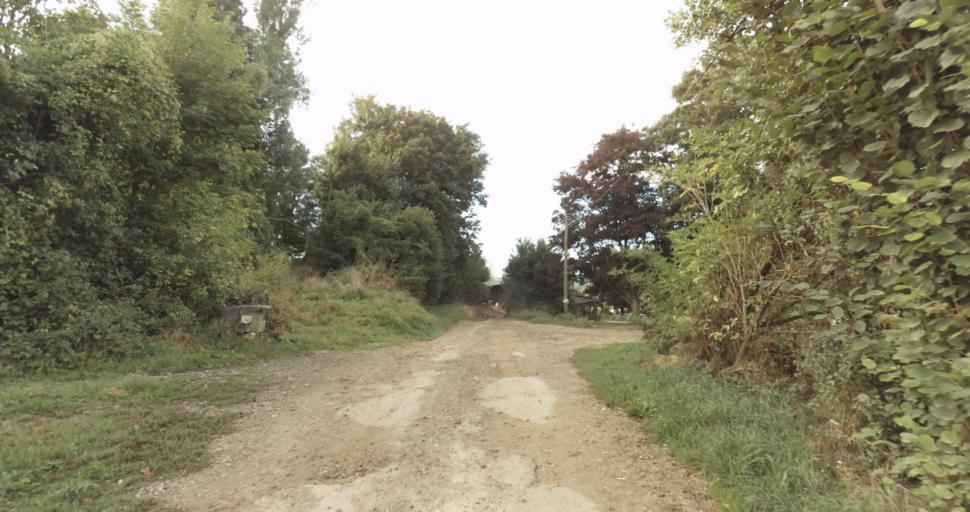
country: FR
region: Lower Normandy
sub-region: Departement de l'Orne
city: Vimoutiers
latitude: 48.8714
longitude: 0.2312
